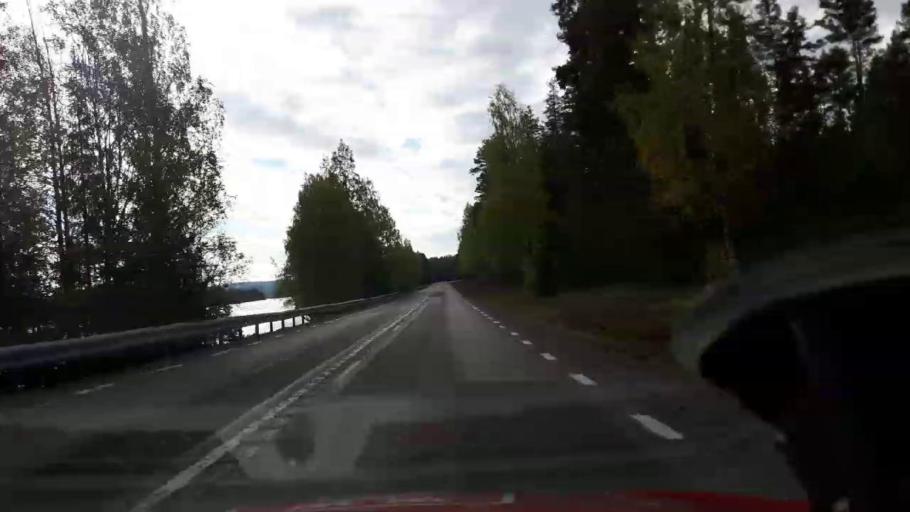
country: SE
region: Gaevleborg
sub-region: Ljusdals Kommun
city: Farila
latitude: 61.9659
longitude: 15.3542
